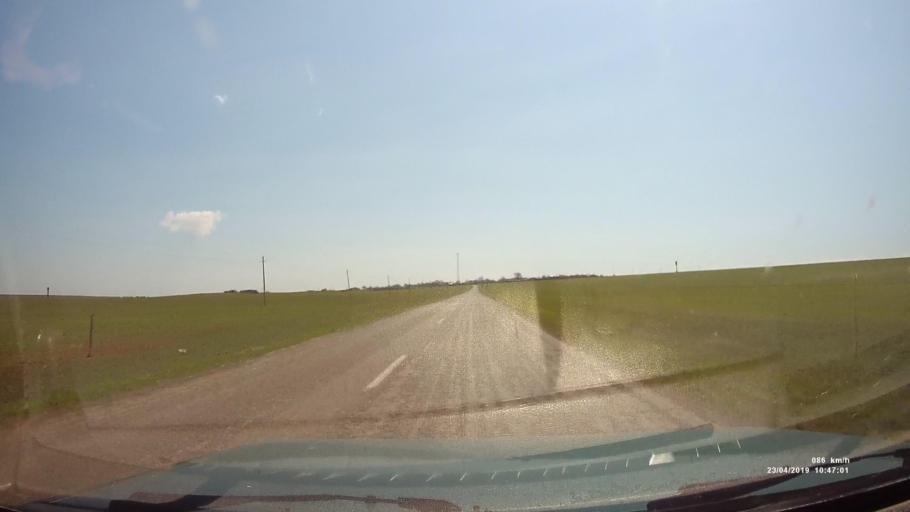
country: RU
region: Kalmykiya
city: Yashalta
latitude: 46.4383
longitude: 42.7005
